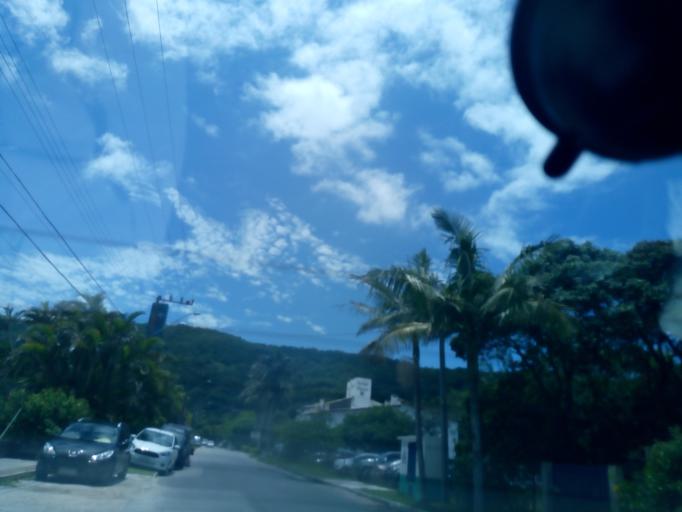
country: BR
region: Santa Catarina
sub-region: Florianopolis
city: Itacorubi
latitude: -27.3906
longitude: -48.4247
